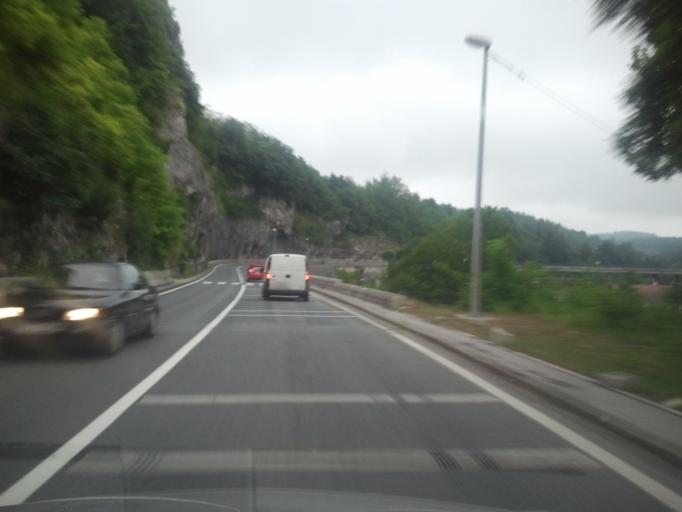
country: HR
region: Karlovacka
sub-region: Grad Karlovac
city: Slunj
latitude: 45.1215
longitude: 15.5860
